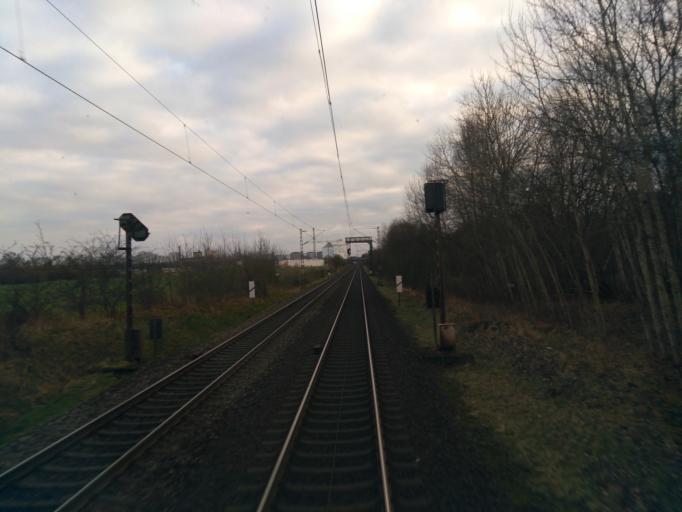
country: DE
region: Lower Saxony
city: Emmendorf
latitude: 52.9929
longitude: 10.5489
